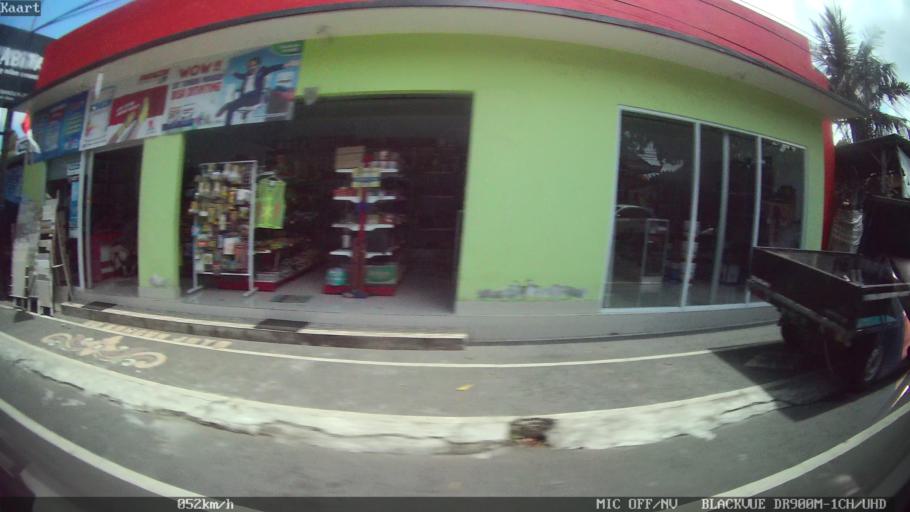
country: ID
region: Bali
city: Banjar Desa
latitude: -8.5878
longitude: 115.2824
